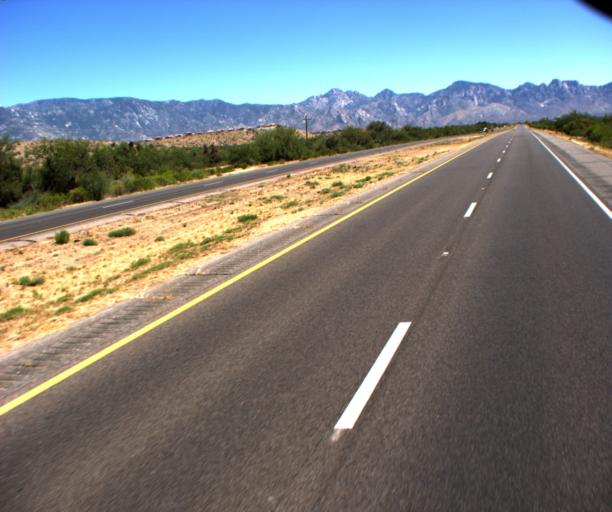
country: US
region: Arizona
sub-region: Pima County
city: Catalina
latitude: 32.5340
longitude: -110.9304
